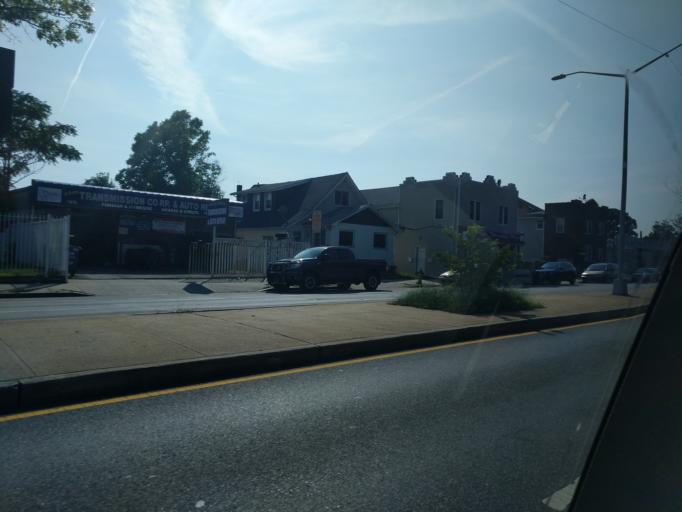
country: US
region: New York
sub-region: Queens County
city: Jamaica
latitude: 40.6843
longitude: -73.7707
